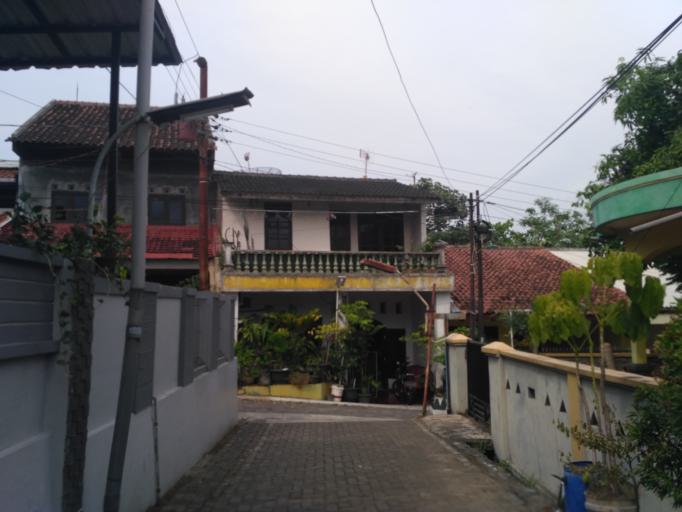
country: ID
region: Central Java
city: Ungaran
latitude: -7.0749
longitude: 110.4329
